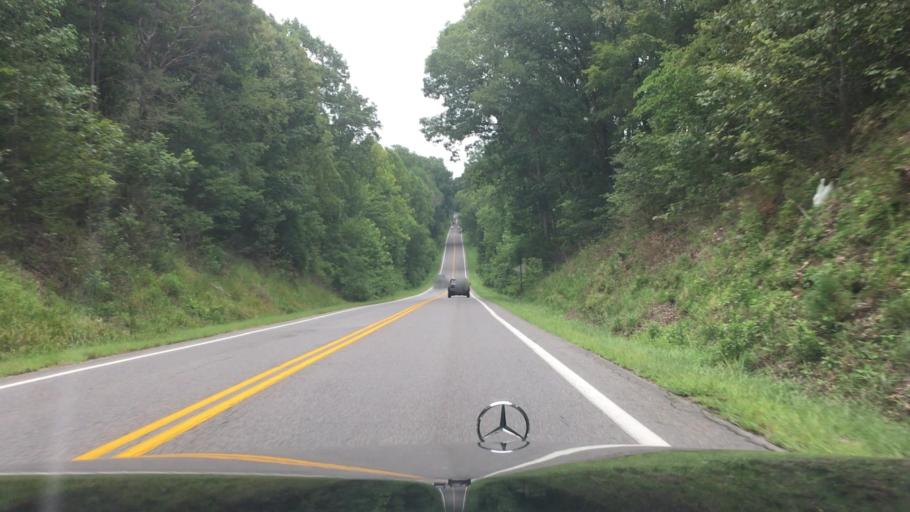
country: US
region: Virginia
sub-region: Prince Edward County
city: Farmville
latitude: 37.2732
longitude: -78.2757
